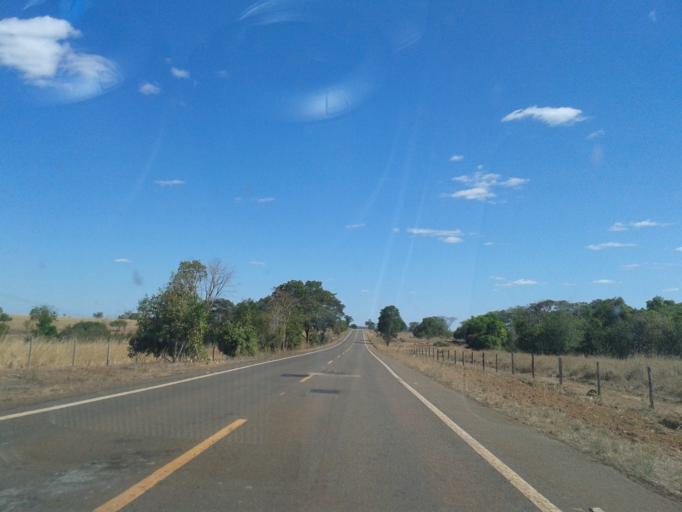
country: BR
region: Goias
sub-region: Sao Miguel Do Araguaia
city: Sao Miguel do Araguaia
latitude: -13.4251
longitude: -50.2768
